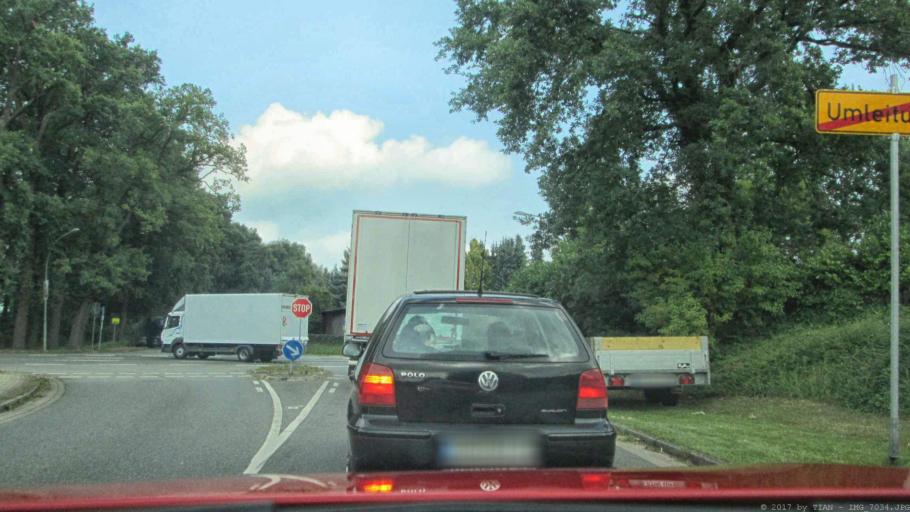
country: DE
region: Lower Saxony
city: Thomasburg
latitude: 53.1965
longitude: 10.6392
